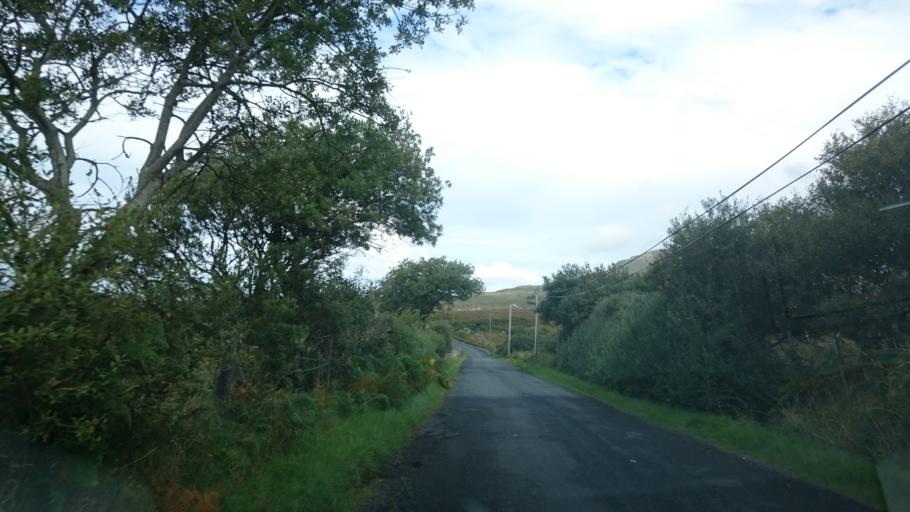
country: IE
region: Connaught
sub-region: Maigh Eo
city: Westport
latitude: 53.9150
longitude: -9.5536
